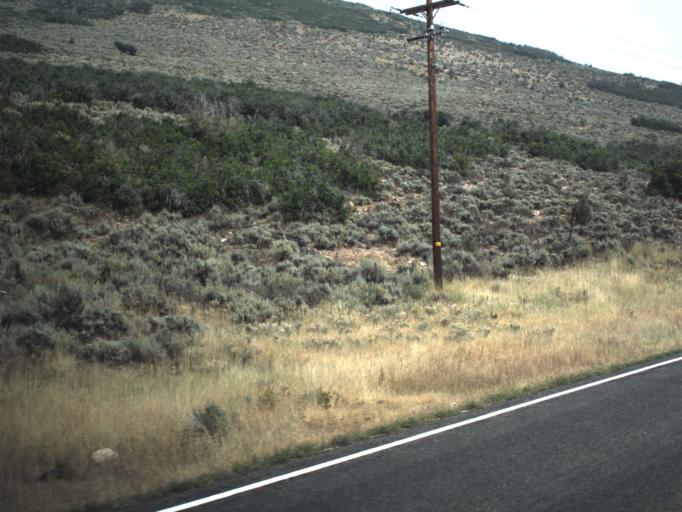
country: US
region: Utah
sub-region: Summit County
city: Kamas
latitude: 40.6385
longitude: -111.2594
